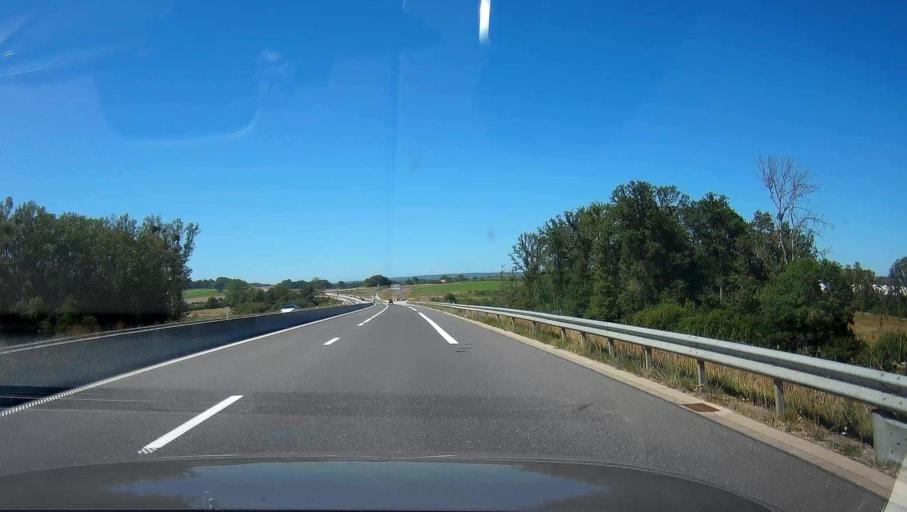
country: FR
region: Champagne-Ardenne
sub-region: Departement des Ardennes
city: Warcq
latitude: 49.7605
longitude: 4.6508
